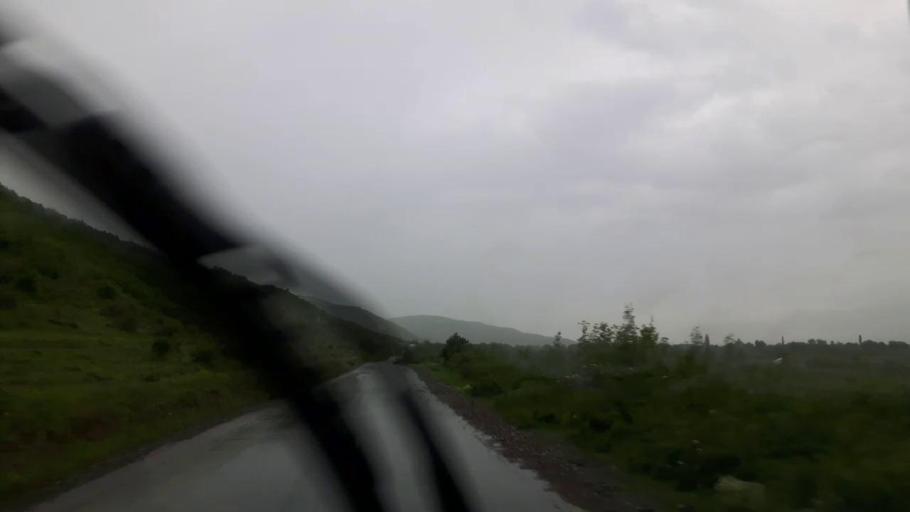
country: GE
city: Agara
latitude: 41.9835
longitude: 43.9287
